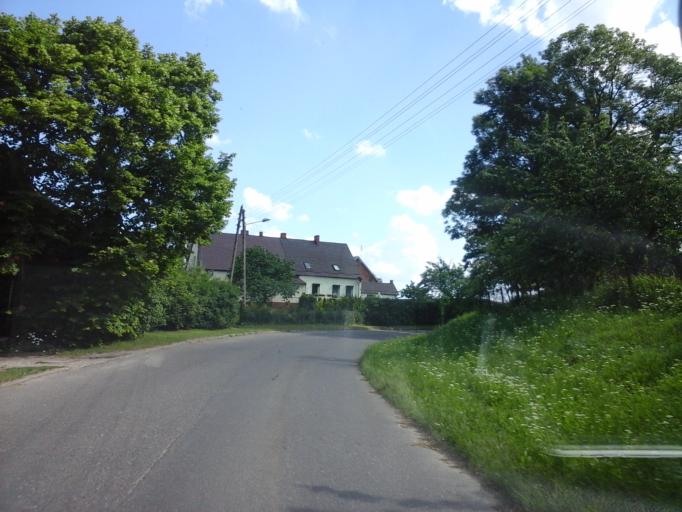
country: PL
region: Lubusz
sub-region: Powiat strzelecko-drezdenecki
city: Dobiegniew
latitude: 53.0189
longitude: 15.7415
